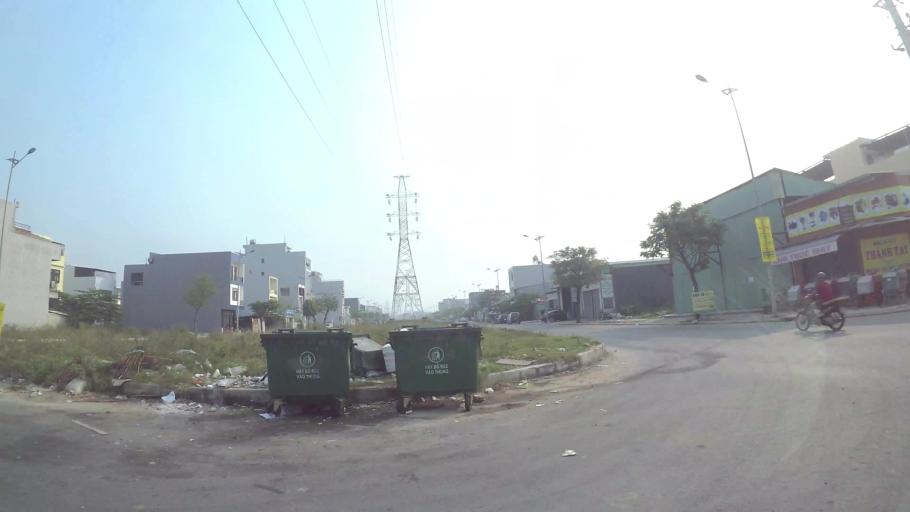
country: VN
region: Da Nang
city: Cam Le
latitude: 16.0091
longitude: 108.2214
